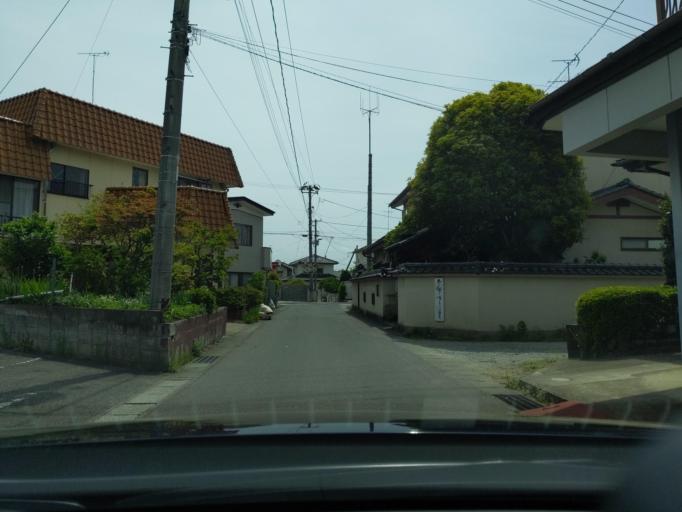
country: JP
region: Fukushima
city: Koriyama
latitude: 37.3925
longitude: 140.3160
